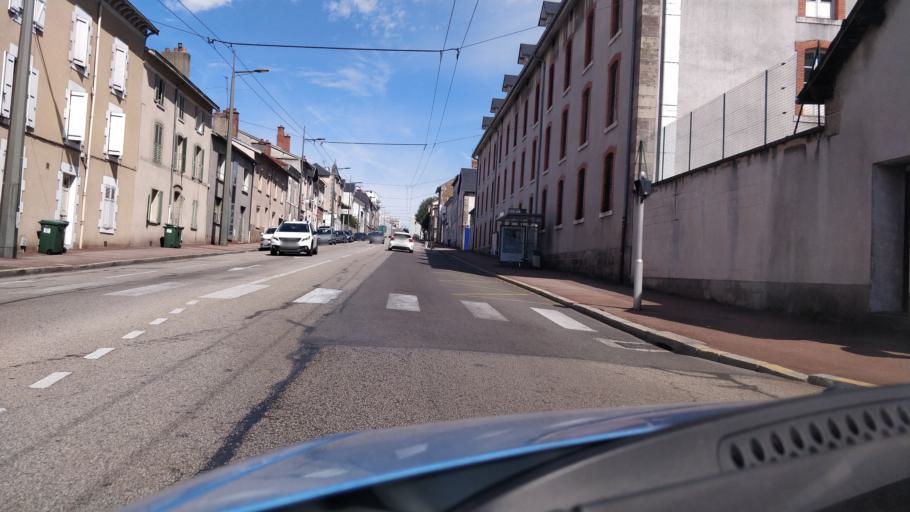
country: FR
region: Limousin
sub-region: Departement de la Haute-Vienne
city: Limoges
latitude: 45.8447
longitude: 1.2601
